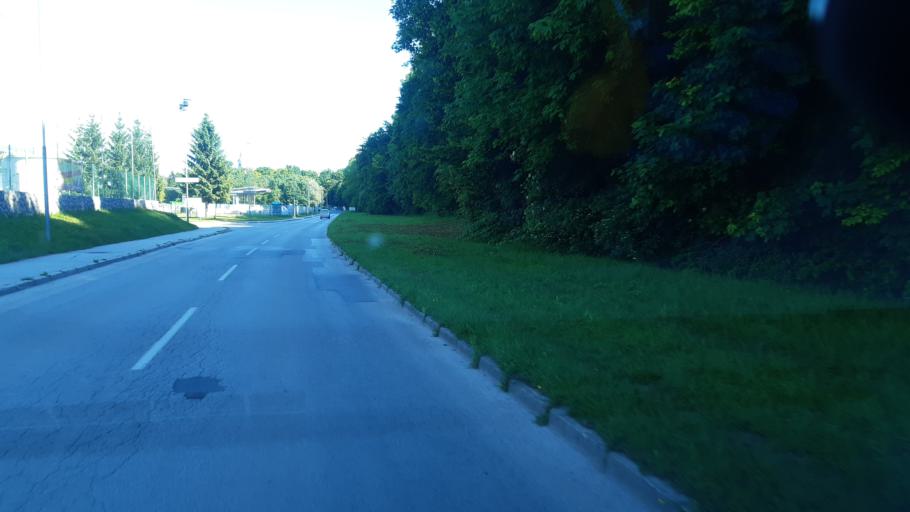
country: SI
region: Kranj
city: Kranj
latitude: 46.2224
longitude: 14.3656
